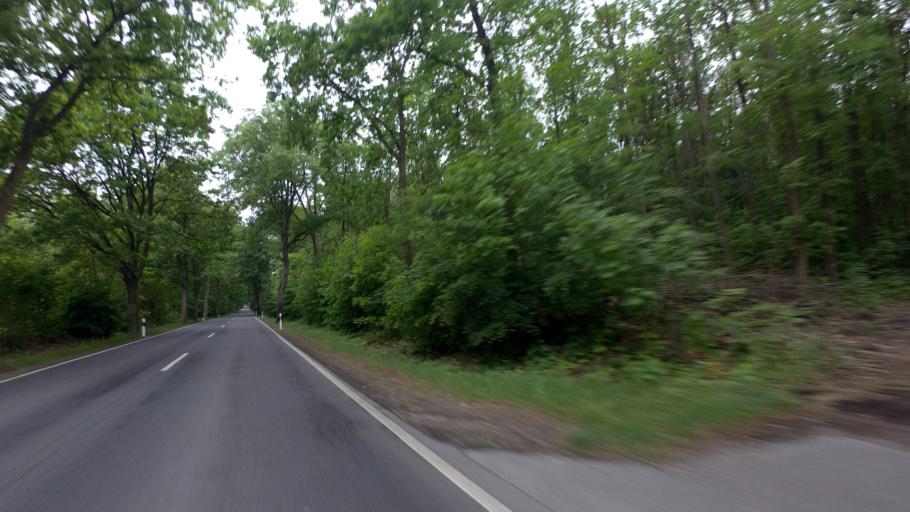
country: DE
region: Brandenburg
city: Marienwerder
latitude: 52.8704
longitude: 13.5383
